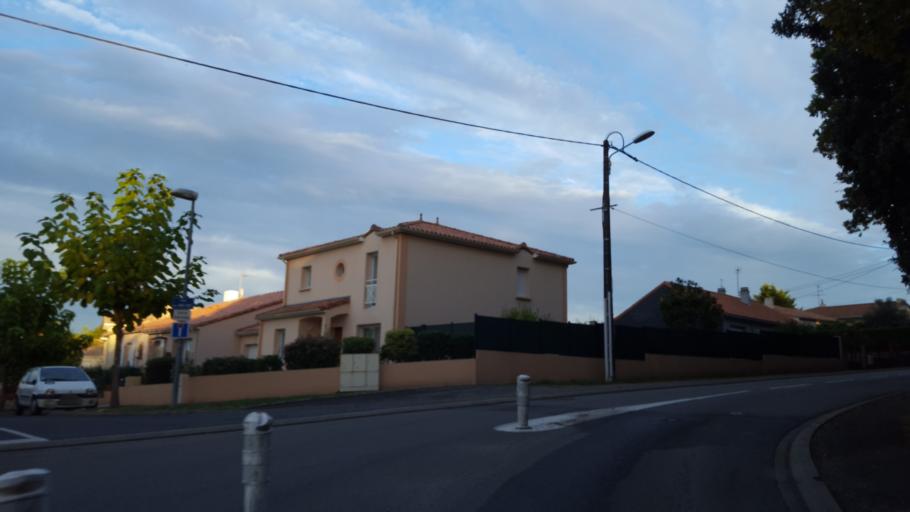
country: FR
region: Pays de la Loire
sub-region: Departement de la Loire-Atlantique
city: Basse-Goulaine
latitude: 47.2130
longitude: -1.4759
